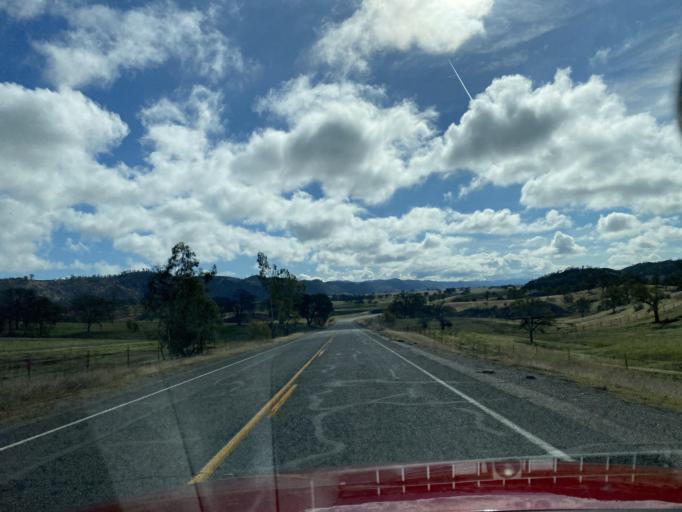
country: US
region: California
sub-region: Glenn County
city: Willows
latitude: 39.5463
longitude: -122.5383
